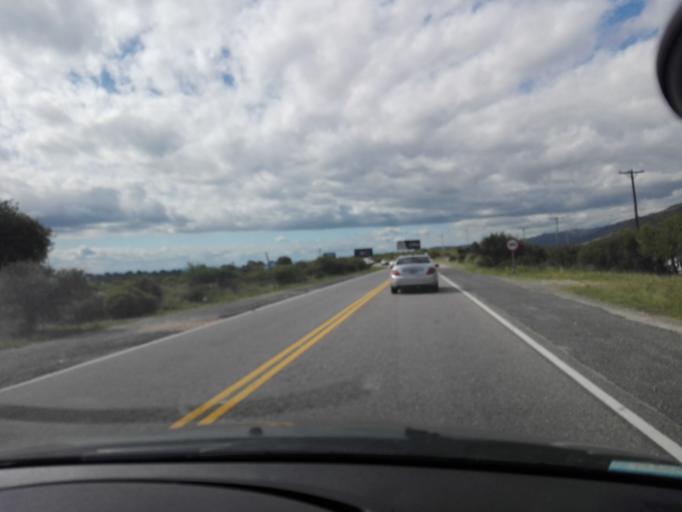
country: AR
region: Cordoba
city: Mina Clavero
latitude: -31.7453
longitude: -64.9338
